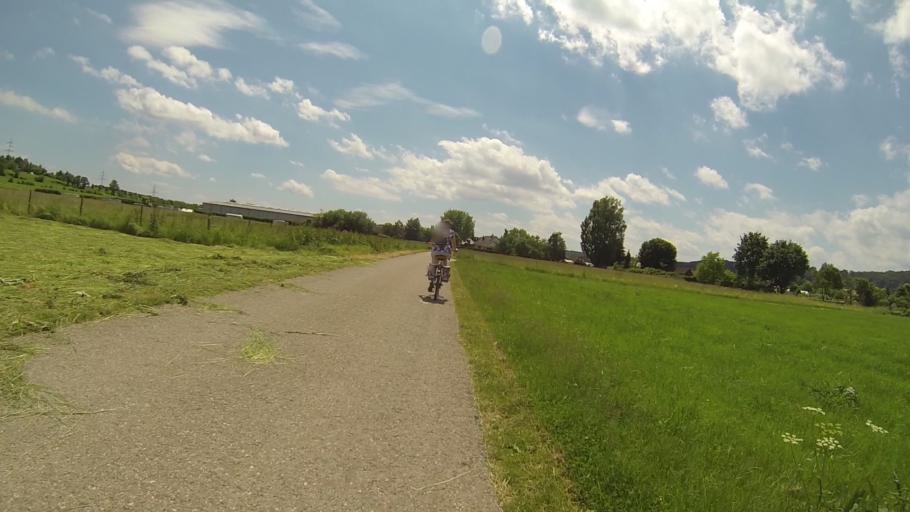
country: DE
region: Baden-Wuerttemberg
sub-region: Regierungsbezirk Stuttgart
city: Bolheim
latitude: 48.6351
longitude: 10.1618
